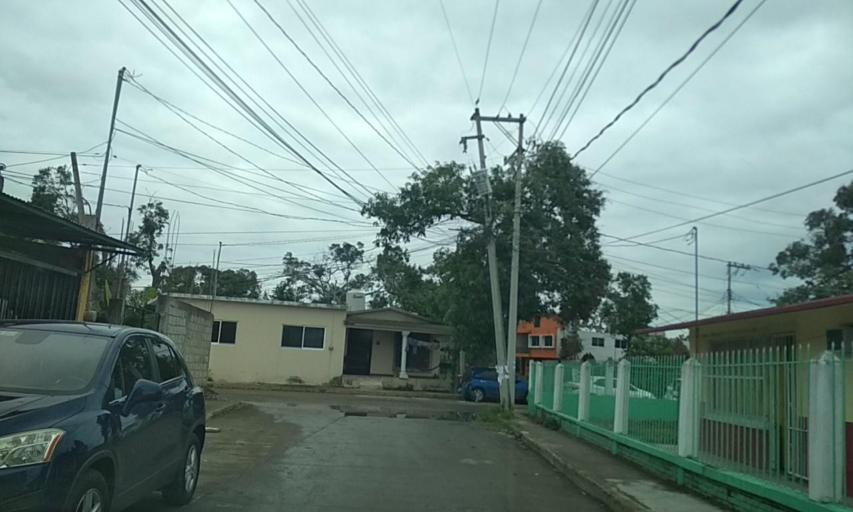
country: MX
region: Veracruz
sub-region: Papantla
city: Residencial Tajin
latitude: 20.5973
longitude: -97.4212
